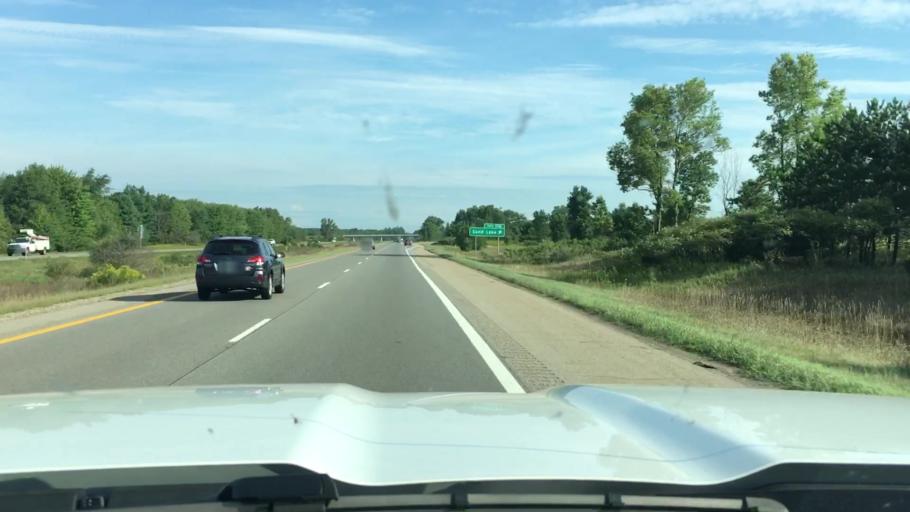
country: US
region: Michigan
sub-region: Kent County
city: Cedar Springs
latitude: 43.2845
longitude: -85.5419
